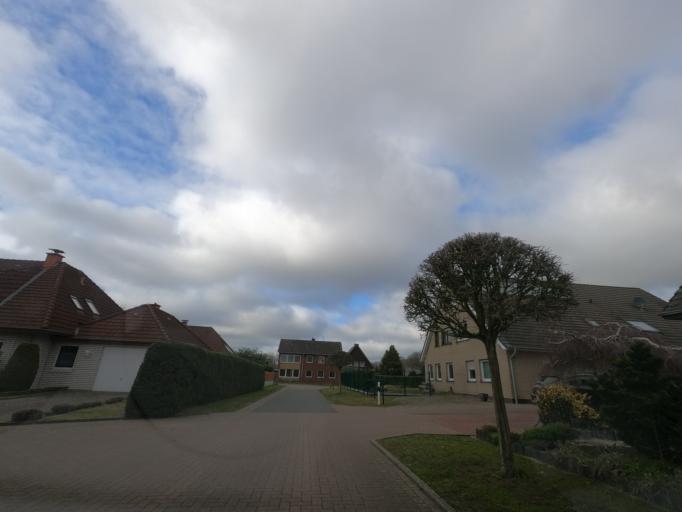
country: DE
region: Lower Saxony
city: Herzlake
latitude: 52.6881
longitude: 7.5940
